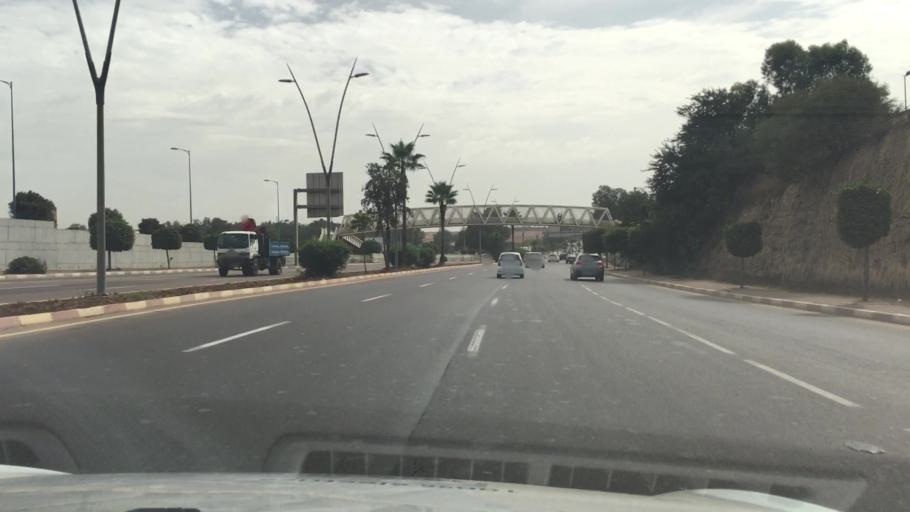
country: MA
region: Grand Casablanca
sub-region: Nouaceur
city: Bouskoura
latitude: 33.5163
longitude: -7.6319
